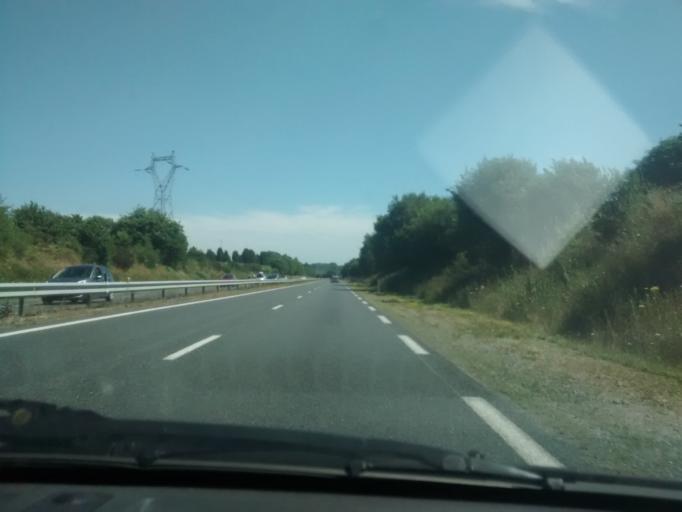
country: FR
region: Brittany
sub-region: Departement des Cotes-d'Armor
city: Plouisy
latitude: 48.5787
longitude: -3.2287
